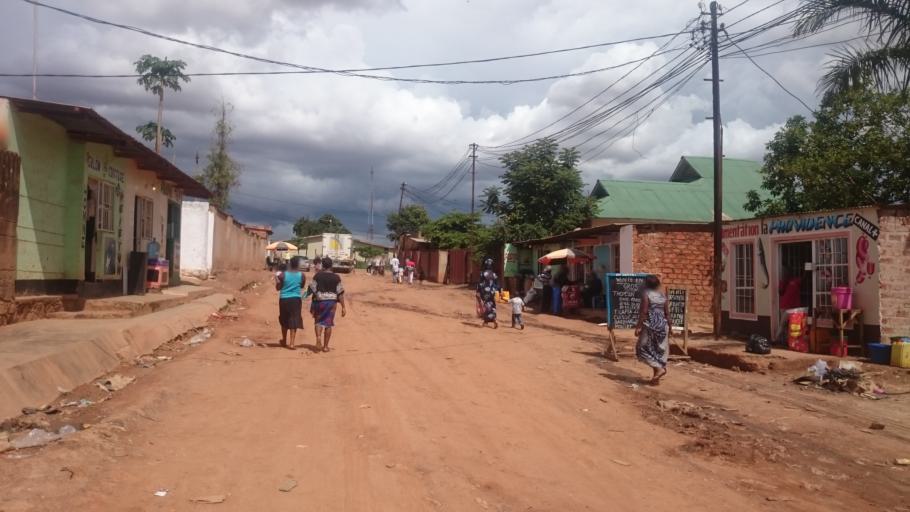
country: CD
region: Katanga
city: Lubumbashi
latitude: -11.6308
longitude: 27.4832
